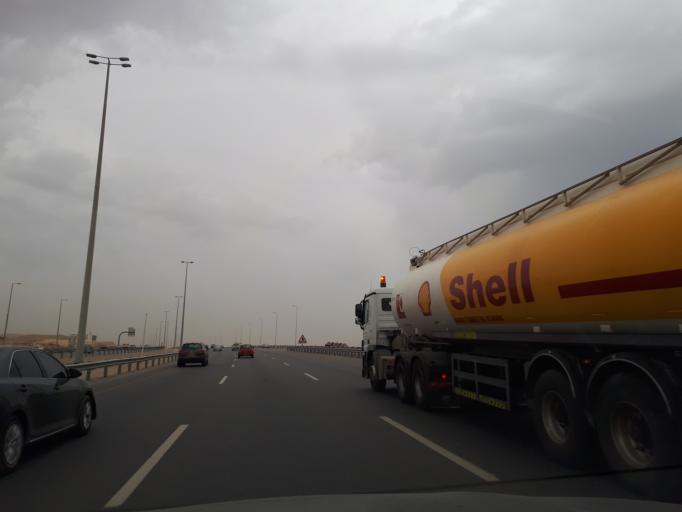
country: OM
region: Muhafazat Masqat
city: Bawshar
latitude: 23.5677
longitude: 58.3746
